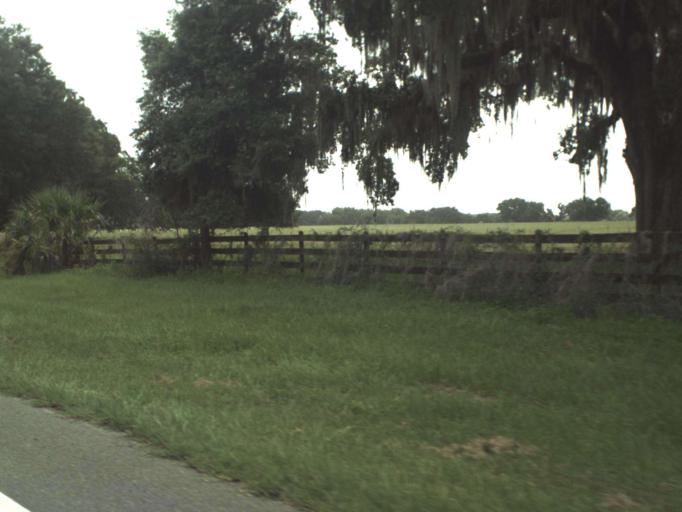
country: US
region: Florida
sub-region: Sumter County
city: Lake Panasoffkee
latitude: 28.7136
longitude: -82.0972
